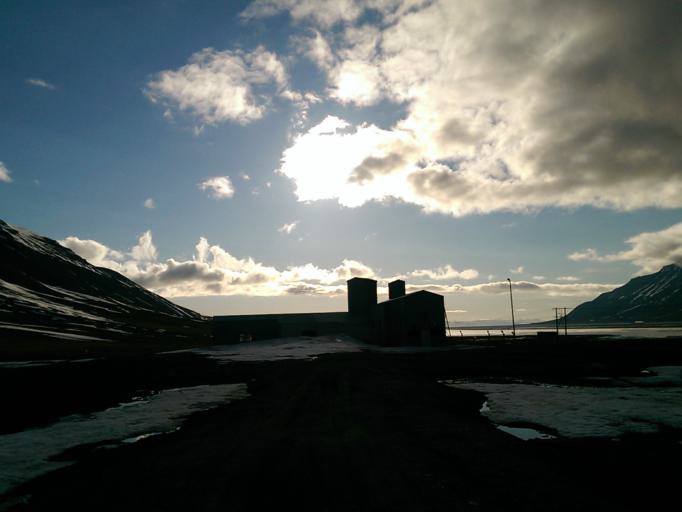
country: SJ
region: Svalbard
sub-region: Spitsbergen
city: Longyearbyen
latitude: 78.1958
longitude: 15.7980
